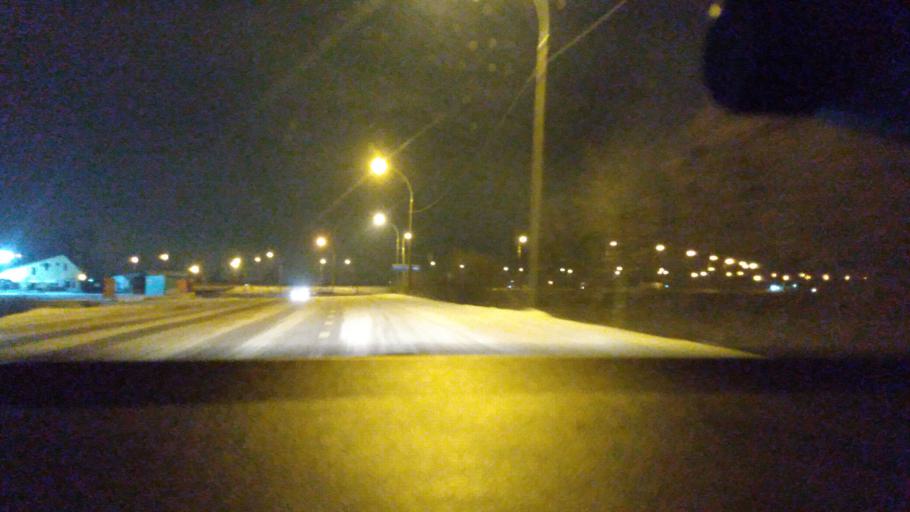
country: RU
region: Moskovskaya
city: Kolomna
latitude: 55.0891
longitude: 38.9103
